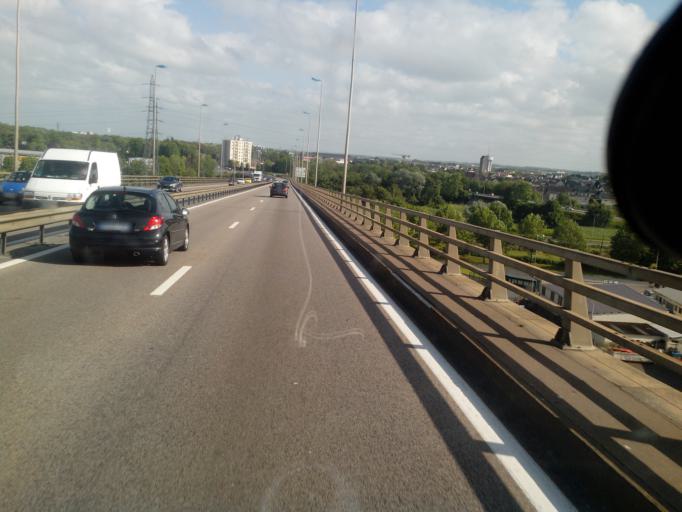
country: FR
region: Lower Normandy
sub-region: Departement du Calvados
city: Mondeville
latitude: 49.1833
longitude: -0.3267
